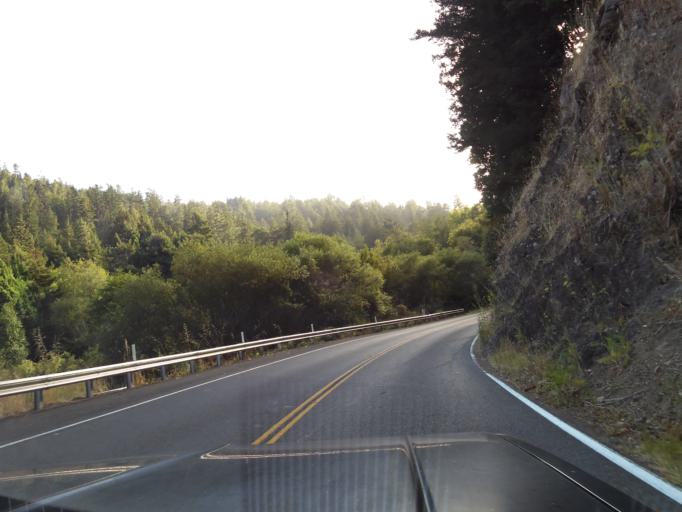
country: US
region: California
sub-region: Mendocino County
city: Fort Bragg
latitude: 39.1717
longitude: -123.6651
